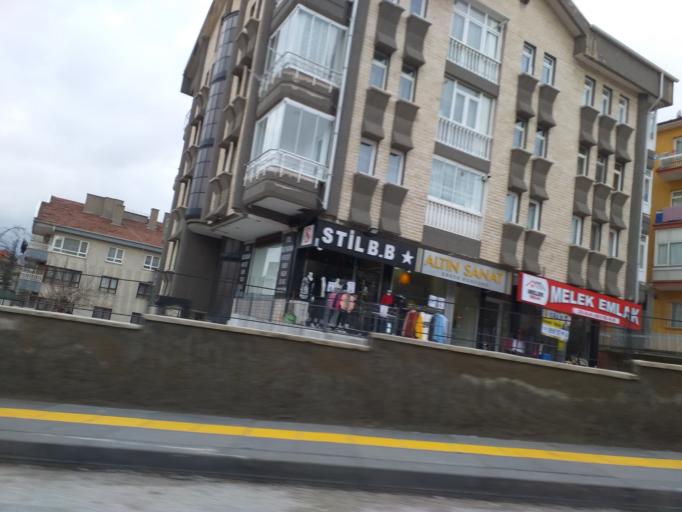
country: TR
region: Ankara
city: Ankara
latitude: 39.9756
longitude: 32.8296
